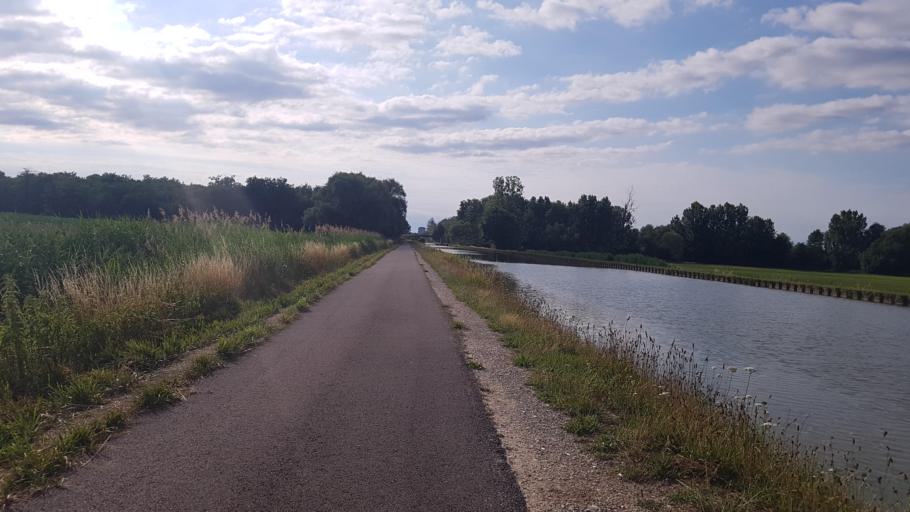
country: FR
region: Alsace
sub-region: Departement du Bas-Rhin
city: Wingersheim
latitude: 48.7349
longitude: 7.6563
